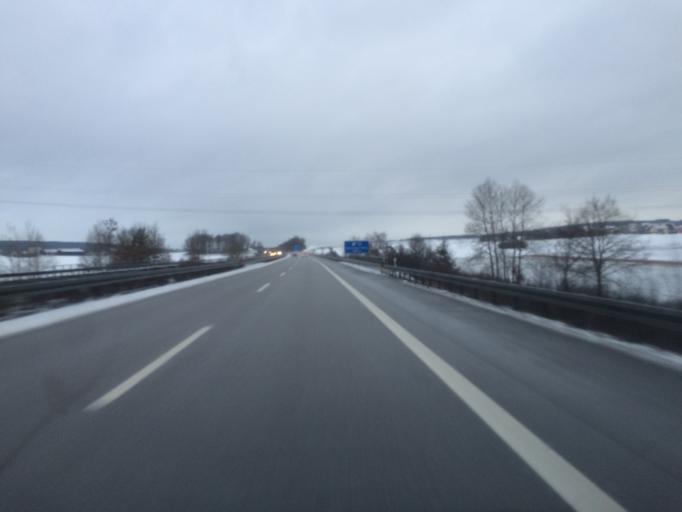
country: DE
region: Bavaria
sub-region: Upper Palatinate
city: Wackersdorf
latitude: 49.3002
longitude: 12.1497
